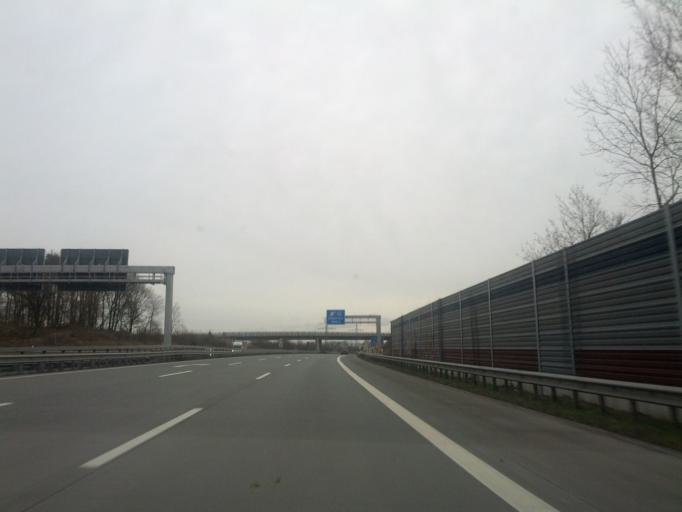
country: DE
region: Lower Saxony
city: Buchholz in der Nordheide
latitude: 53.3729
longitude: 9.8619
